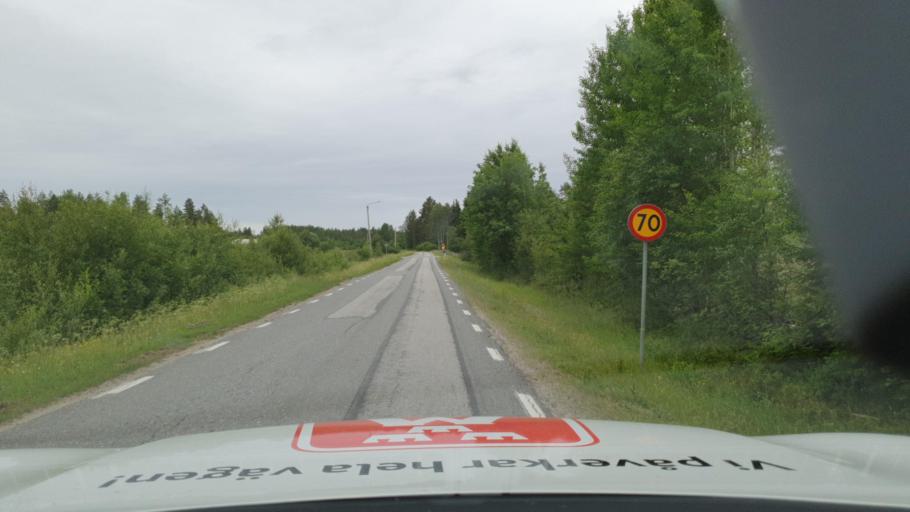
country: SE
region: Vaesterbotten
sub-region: Nordmalings Kommun
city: Nordmaling
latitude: 63.5043
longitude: 19.4172
